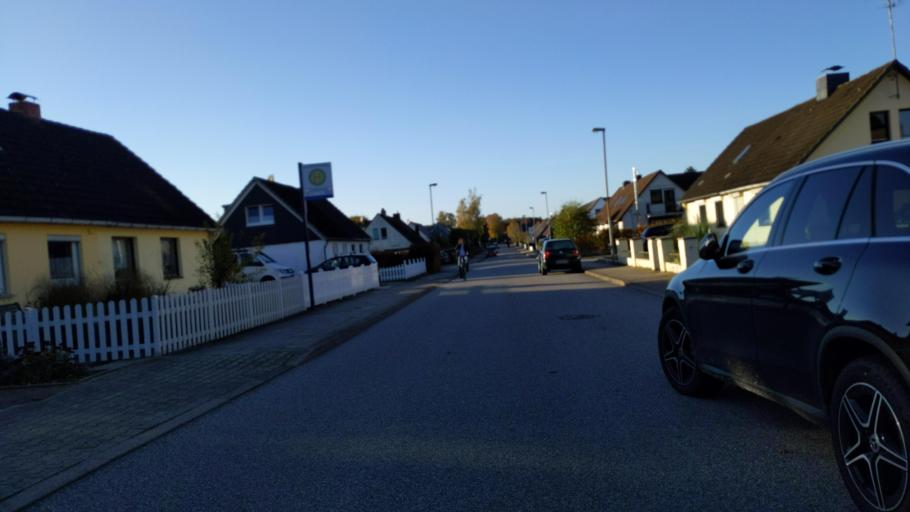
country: DE
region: Schleswig-Holstein
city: Gross Gronau
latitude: 53.8303
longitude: 10.7259
